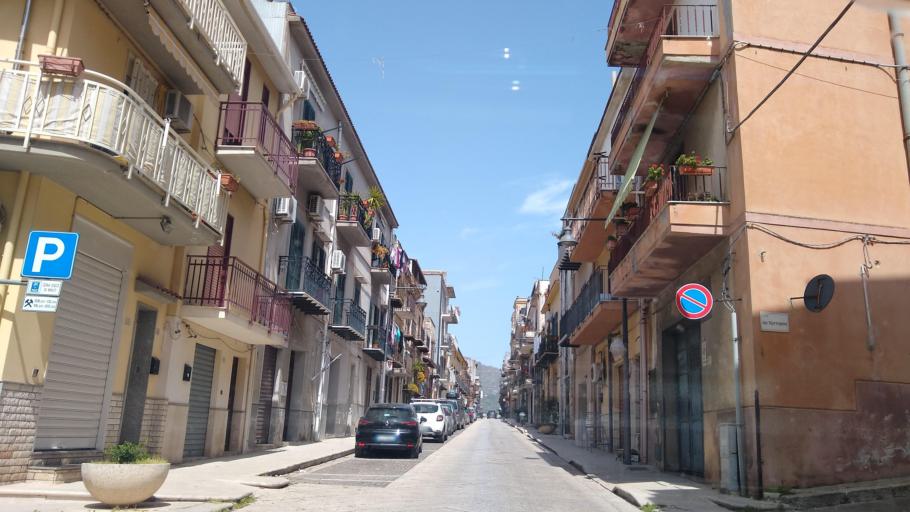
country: IT
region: Sicily
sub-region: Palermo
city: San Giuseppe Jato
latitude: 37.9714
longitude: 13.1838
